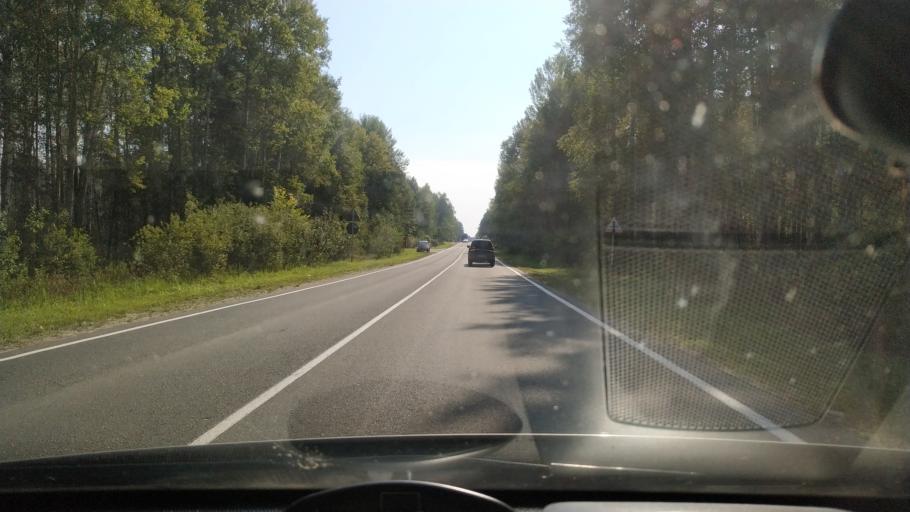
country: RU
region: Rjazan
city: Spas-Klepiki
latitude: 55.2249
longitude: 40.0669
